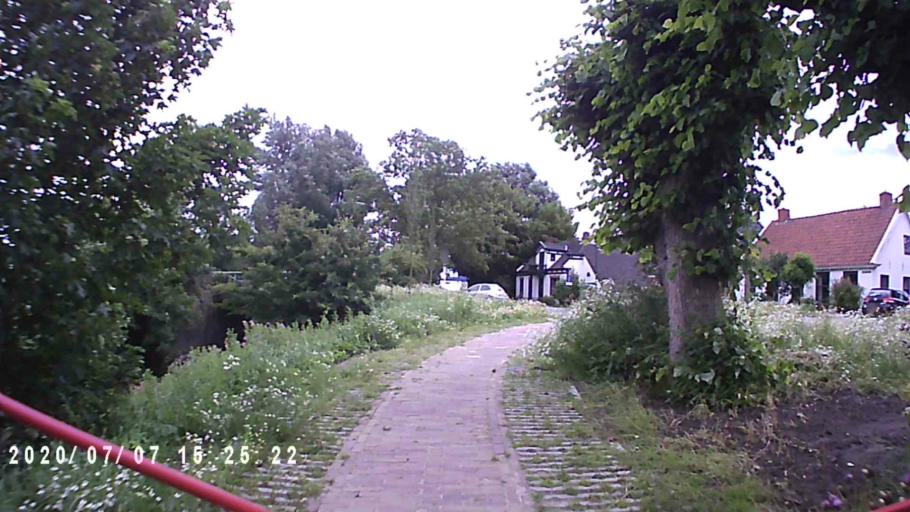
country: NL
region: Groningen
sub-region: Gemeente Winsum
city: Winsum
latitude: 53.3503
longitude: 6.4678
